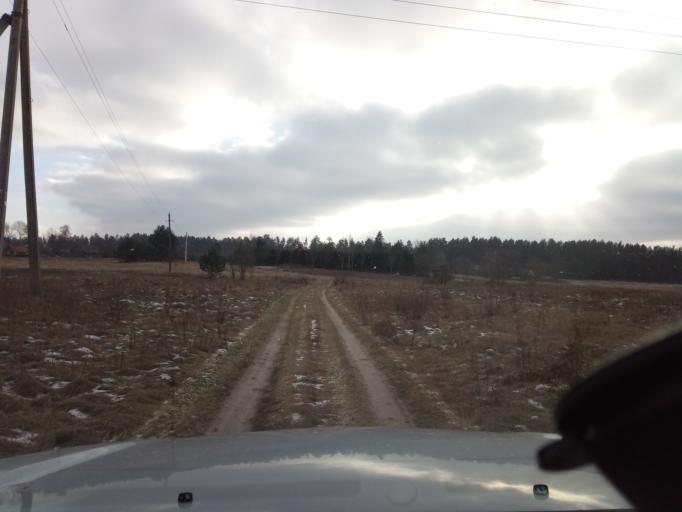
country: LT
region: Alytaus apskritis
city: Druskininkai
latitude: 54.1136
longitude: 24.2193
